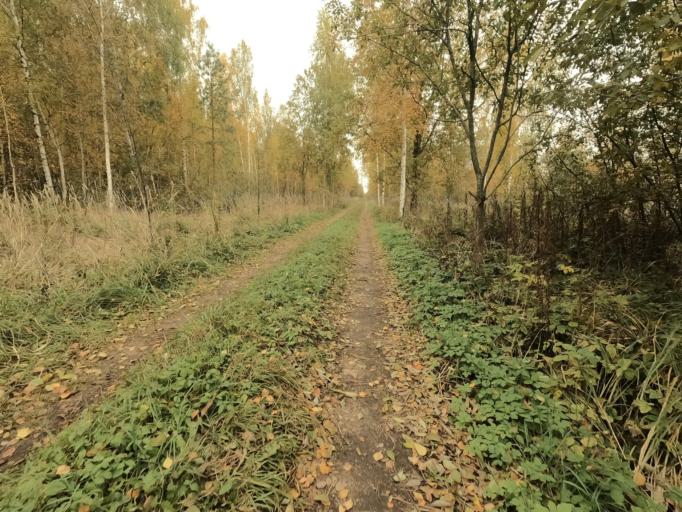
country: RU
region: Novgorod
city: Pankovka
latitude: 58.8777
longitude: 30.9412
